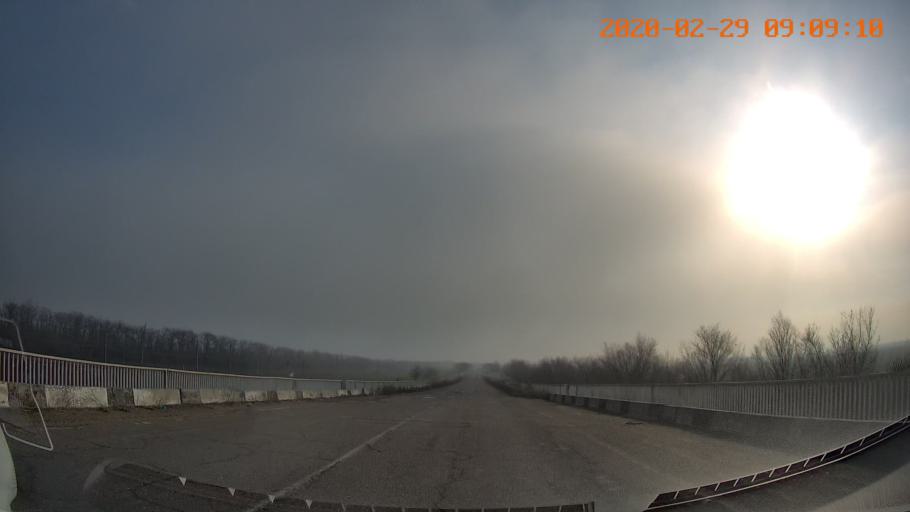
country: MD
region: Telenesti
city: Slobozia
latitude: 46.8452
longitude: 29.7587
